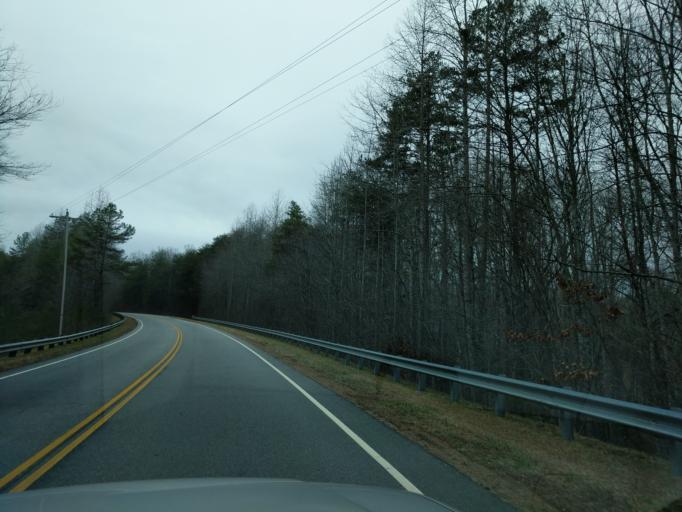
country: US
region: South Carolina
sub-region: Greenville County
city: Slater-Marietta
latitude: 35.0841
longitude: -82.4895
